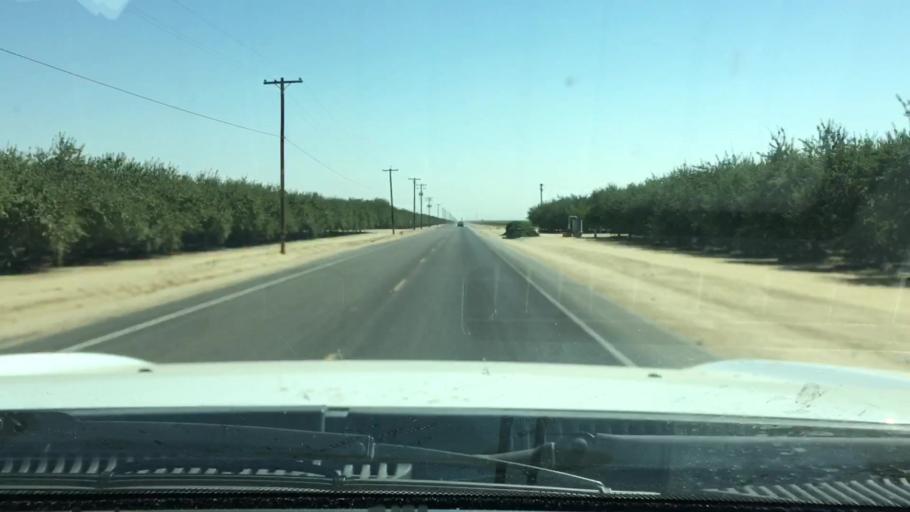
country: US
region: California
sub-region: Kern County
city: Wasco
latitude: 35.5582
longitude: -119.3199
